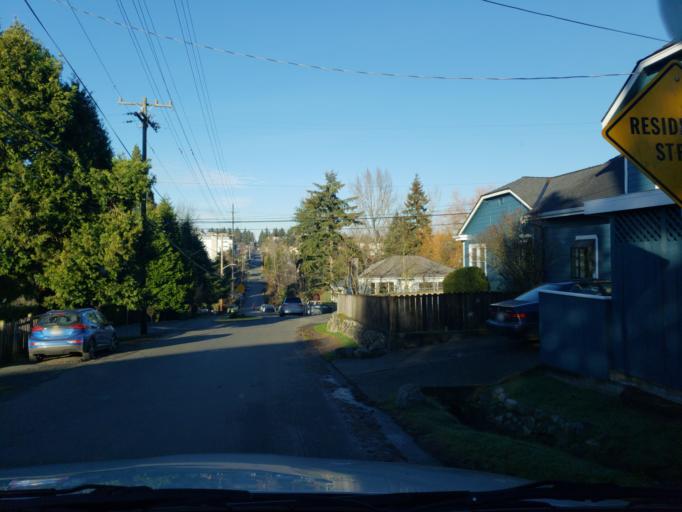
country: US
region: Washington
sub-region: King County
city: Shoreline
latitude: 47.7037
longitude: -122.3205
